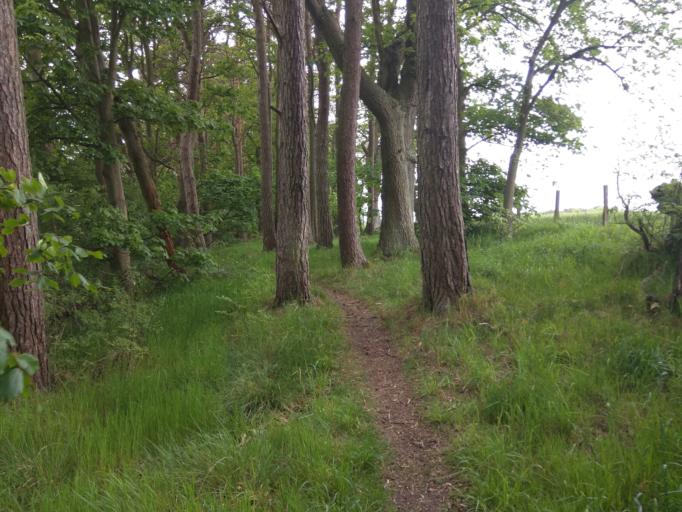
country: GB
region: Scotland
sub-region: Edinburgh
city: Balerno
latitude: 55.8780
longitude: -3.3527
